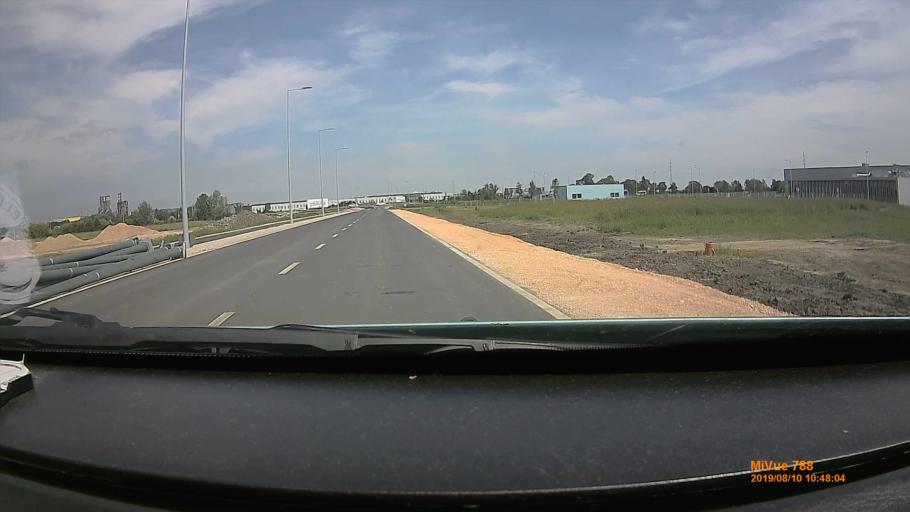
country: HU
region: Borsod-Abauj-Zemplen
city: Malyi
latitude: 48.0527
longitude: 20.8100
